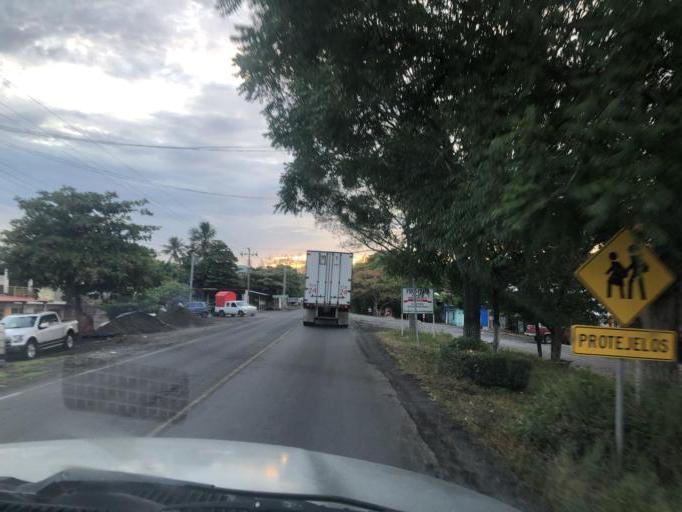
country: MX
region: Veracruz
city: Villa Emilio Carranza
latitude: 19.8908
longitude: -96.5064
